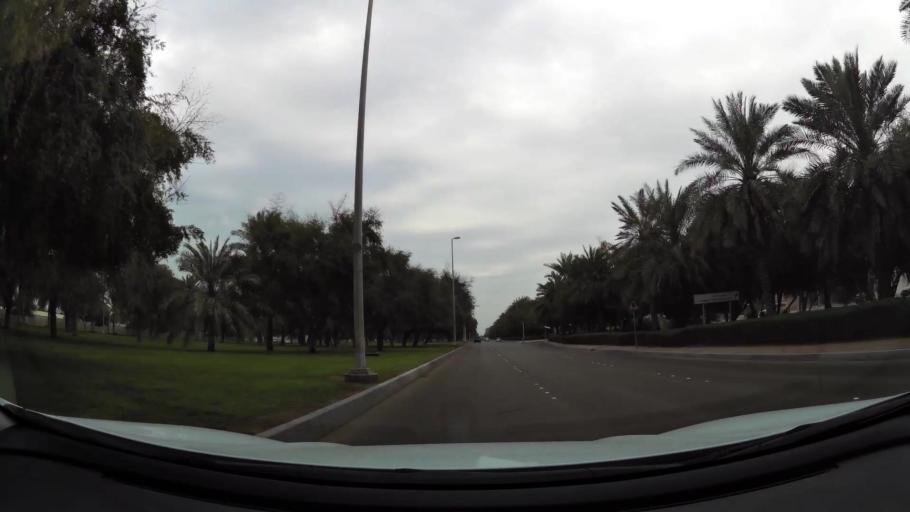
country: AE
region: Abu Dhabi
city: Abu Dhabi
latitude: 24.4396
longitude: 54.3835
